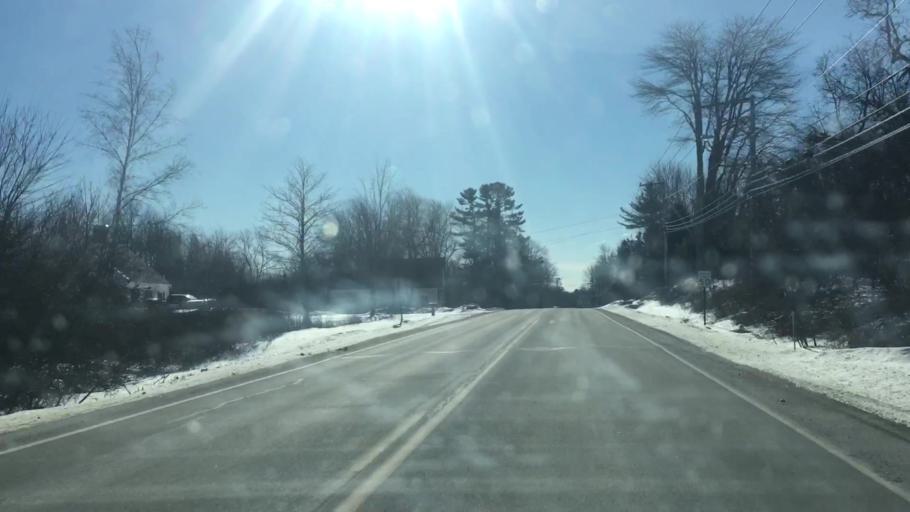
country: US
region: Maine
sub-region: Hancock County
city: Ellsworth
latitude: 44.5059
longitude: -68.4399
